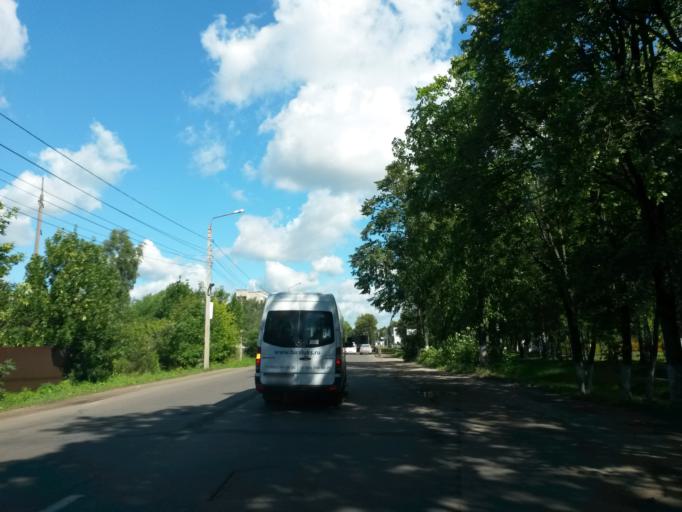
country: RU
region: Jaroslavl
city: Yaroslavl
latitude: 57.5910
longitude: 39.8775
